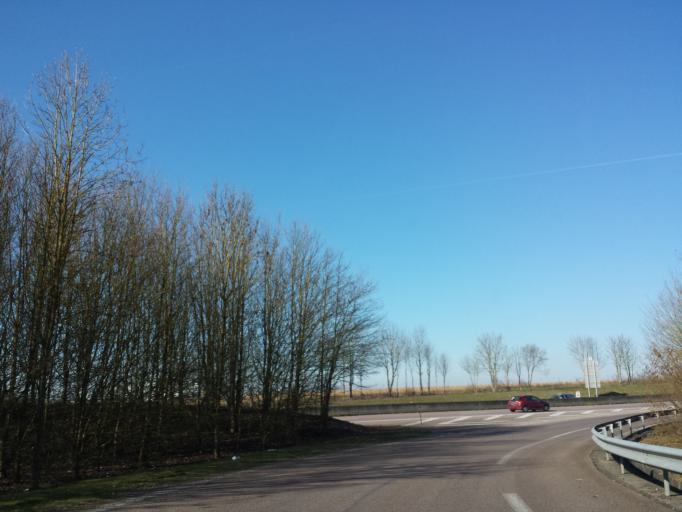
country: FR
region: Picardie
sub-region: Departement de l'Oise
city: Lormaison
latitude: 49.2473
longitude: 2.0957
